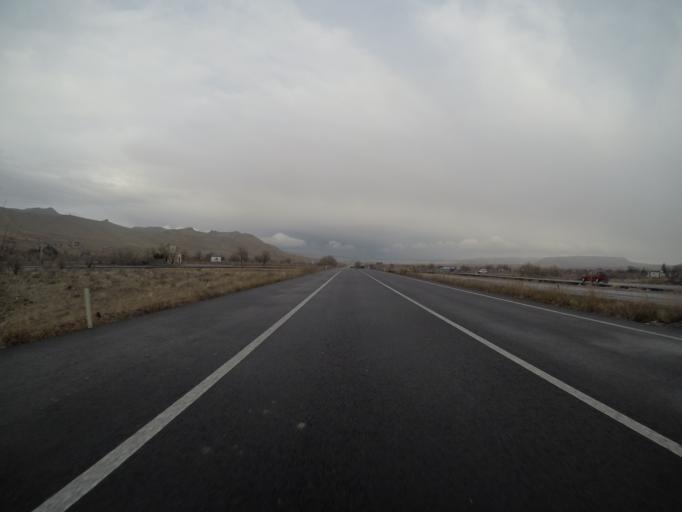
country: TR
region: Nevsehir
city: Goereme
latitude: 38.6791
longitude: 34.7876
